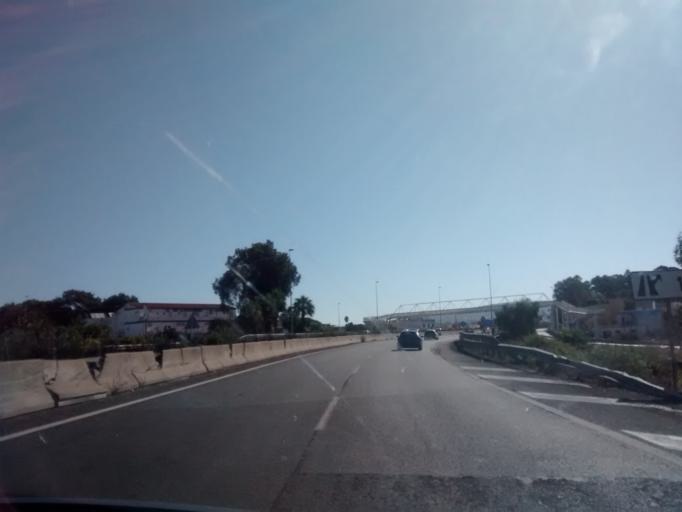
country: ES
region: Andalusia
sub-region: Provincia de Cadiz
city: San Roque
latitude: 36.2031
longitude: -5.4223
